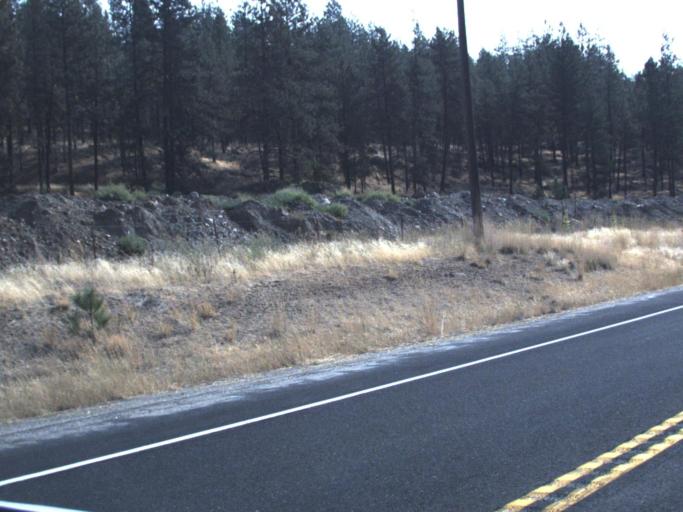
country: US
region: Washington
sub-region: Spokane County
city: Fairwood
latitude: 47.7608
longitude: -117.5349
